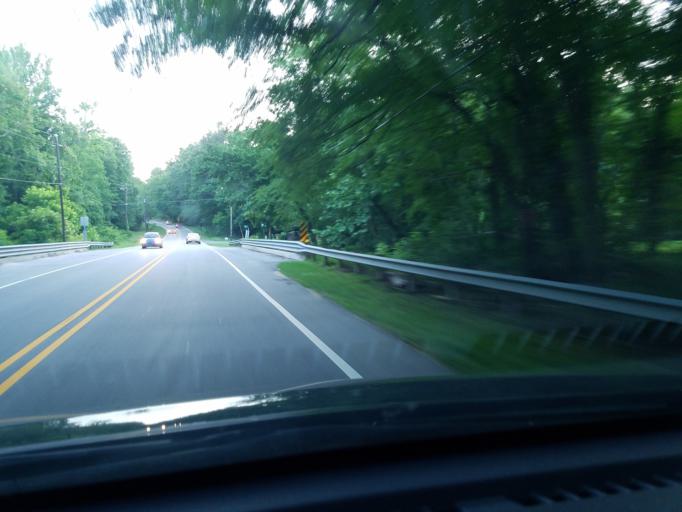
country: US
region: North Carolina
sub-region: Durham County
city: Durham
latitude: 35.9351
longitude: -78.9483
